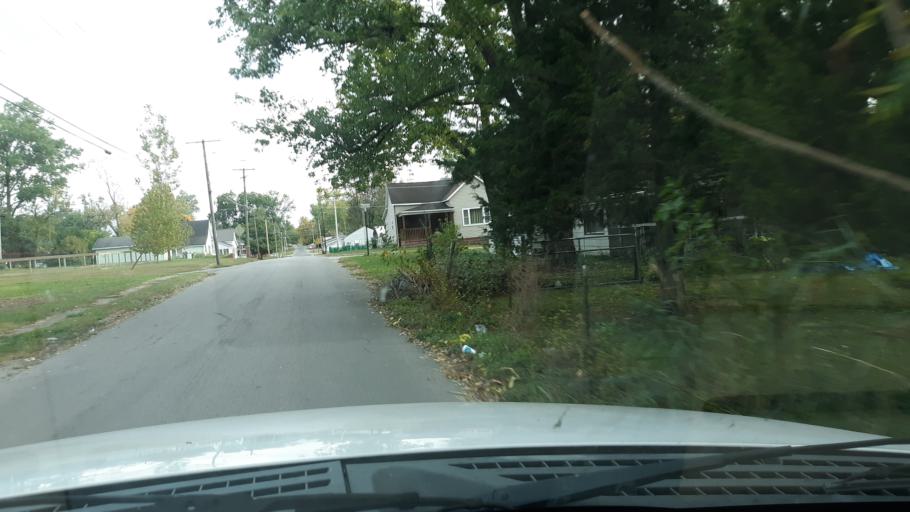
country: US
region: Illinois
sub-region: Saline County
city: Eldorado
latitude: 37.8144
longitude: -88.4337
